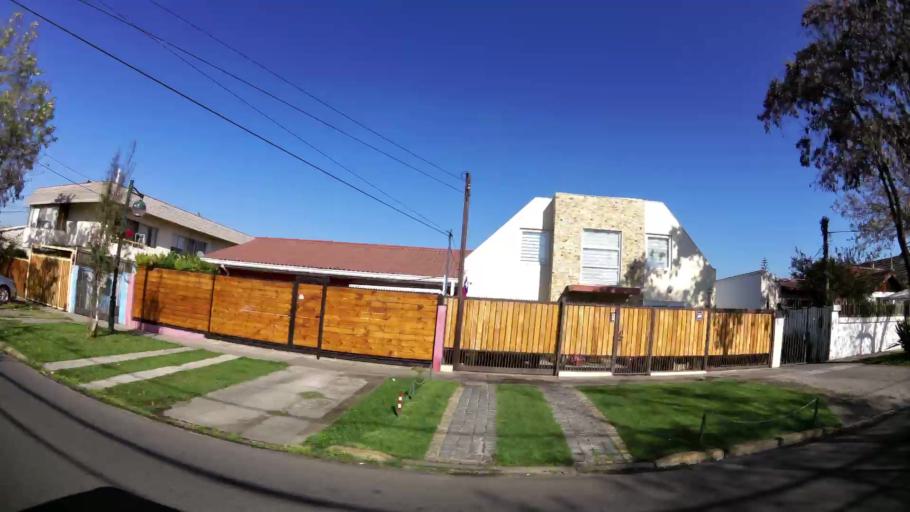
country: CL
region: Santiago Metropolitan
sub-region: Provincia de Santiago
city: Villa Presidente Frei, Nunoa, Santiago, Chile
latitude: -33.4436
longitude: -70.5814
